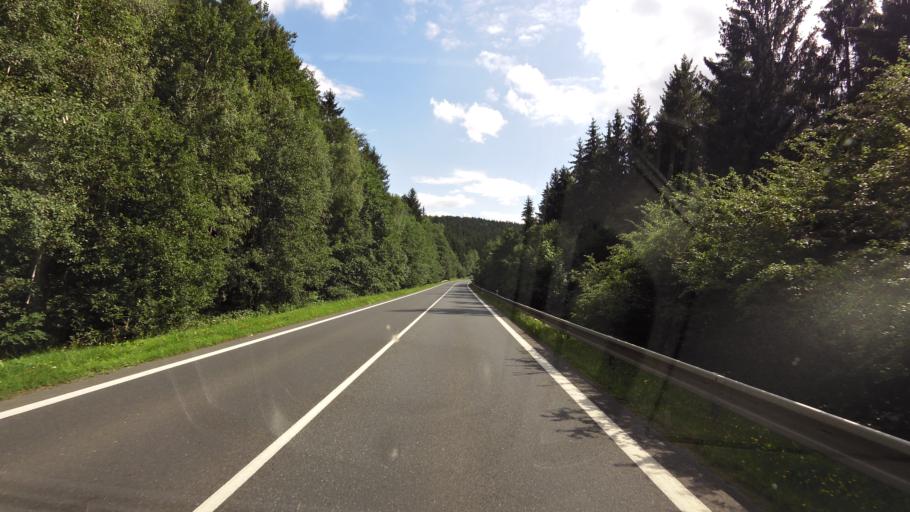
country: DE
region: Bavaria
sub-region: Upper Palatinate
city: Furth im Wald
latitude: 49.3692
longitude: 12.8516
